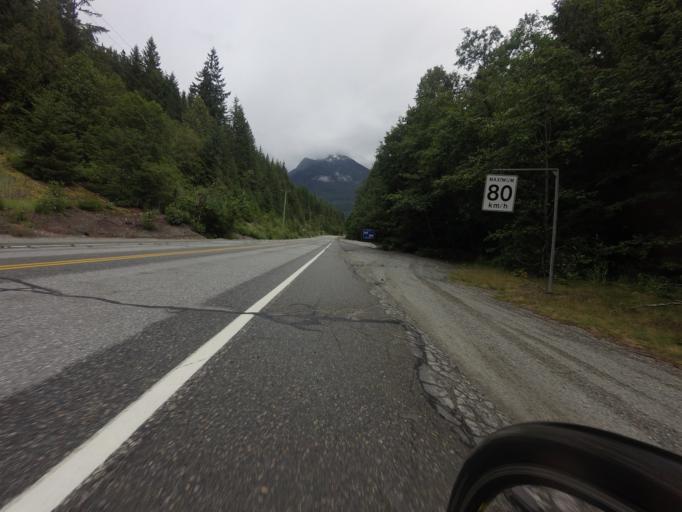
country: CA
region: British Columbia
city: Whistler
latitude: 50.1706
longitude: -122.9144
